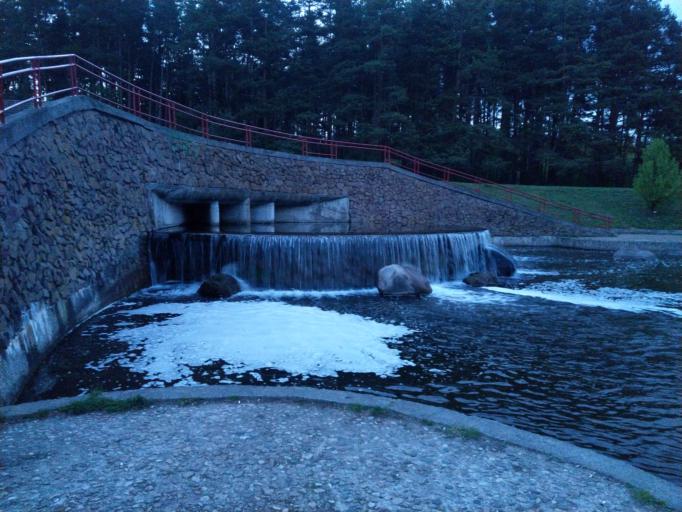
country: BY
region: Minsk
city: Bal'shavik
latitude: 53.9532
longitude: 27.5710
